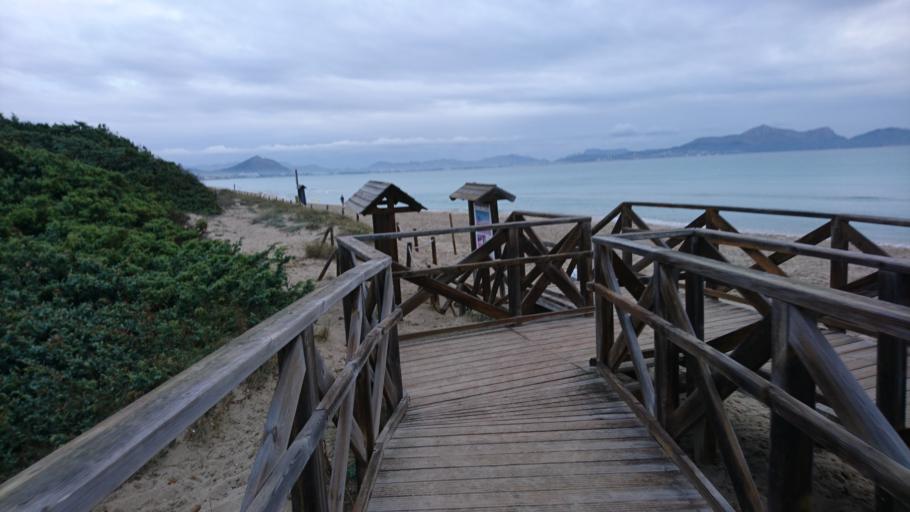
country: ES
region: Balearic Islands
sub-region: Illes Balears
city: Port d'Alcudia
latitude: 39.7759
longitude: 3.1422
